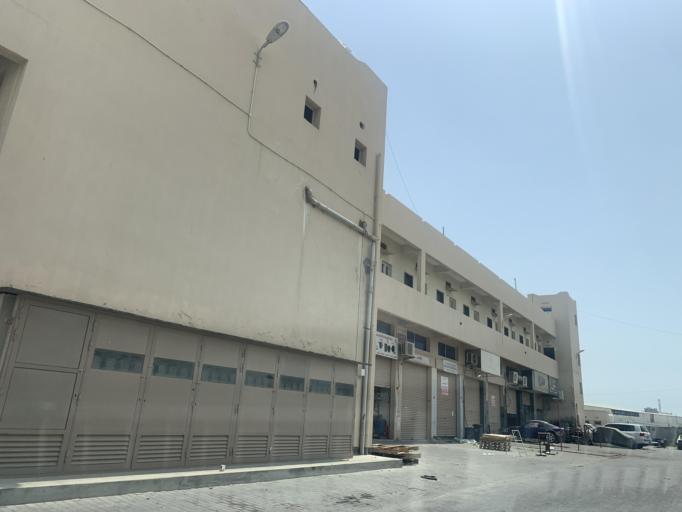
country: BH
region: Central Governorate
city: Madinat Hamad
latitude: 26.1421
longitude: 50.4894
